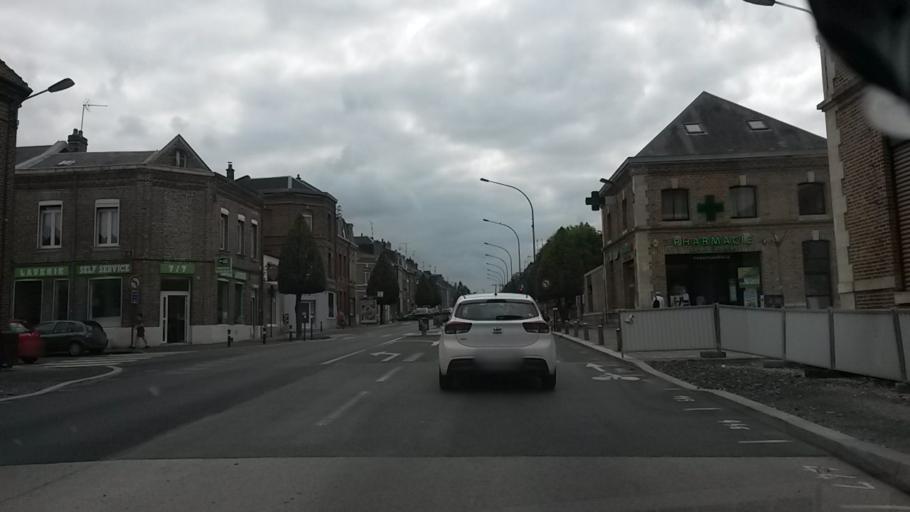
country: FR
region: Picardie
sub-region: Departement de la Somme
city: Amiens
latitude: 49.8896
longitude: 2.2816
